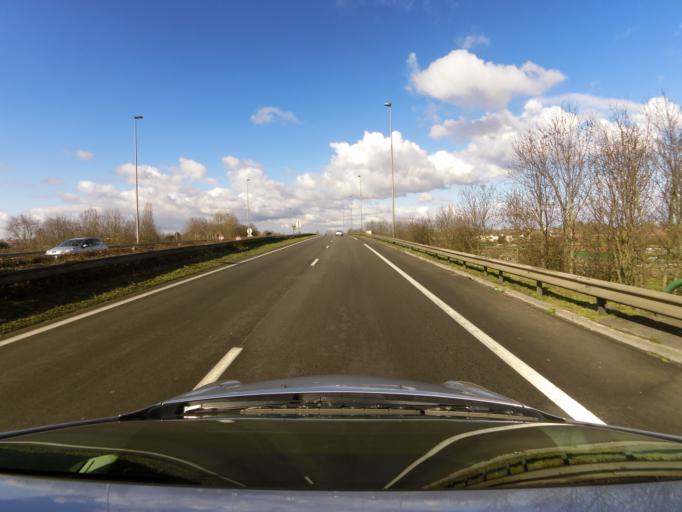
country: FR
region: Nord-Pas-de-Calais
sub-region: Departement du Nord
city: Saint-Pol-sur-Mer
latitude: 51.0112
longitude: 2.3362
